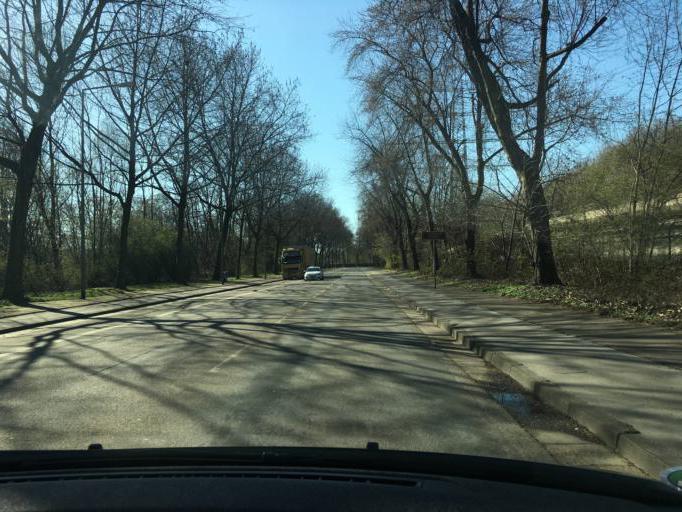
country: DE
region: North Rhine-Westphalia
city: Meiderich
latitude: 51.5071
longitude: 6.7430
